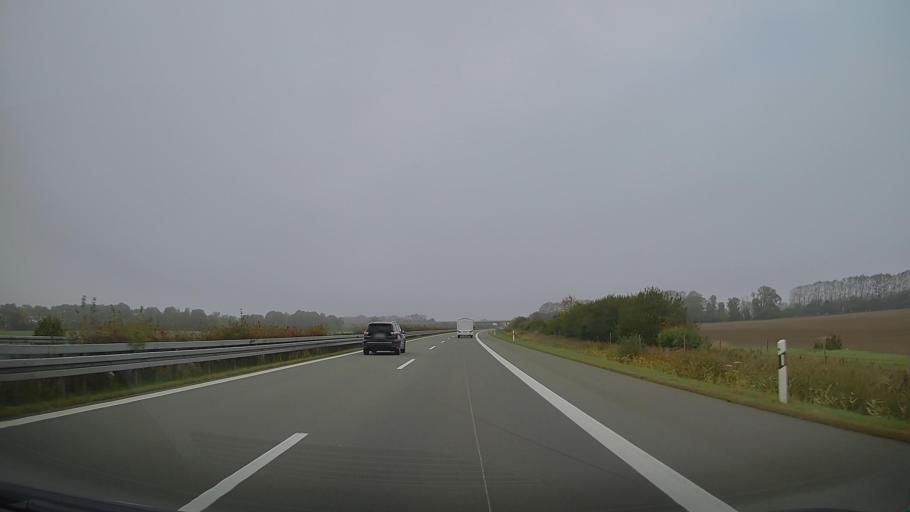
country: DE
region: Mecklenburg-Vorpommern
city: Grimmen
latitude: 54.0782
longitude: 12.9329
